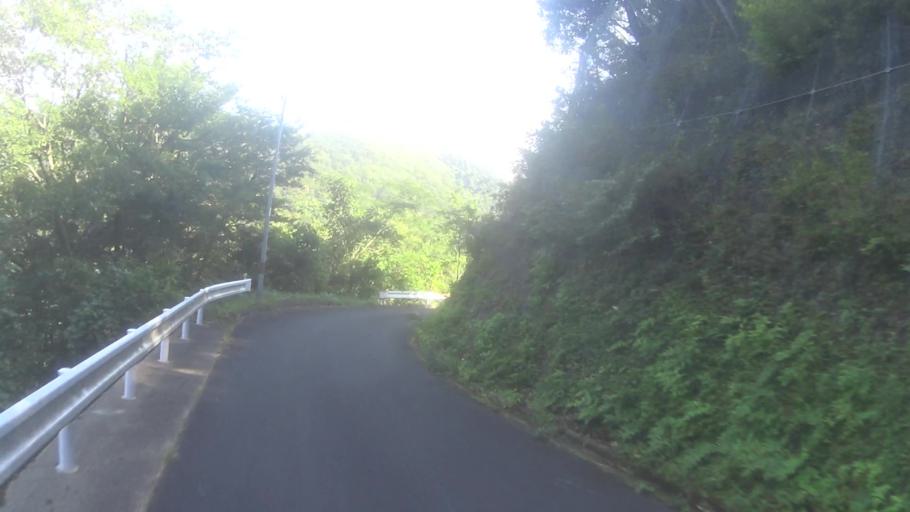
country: JP
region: Kyoto
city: Miyazu
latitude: 35.7028
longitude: 135.1561
